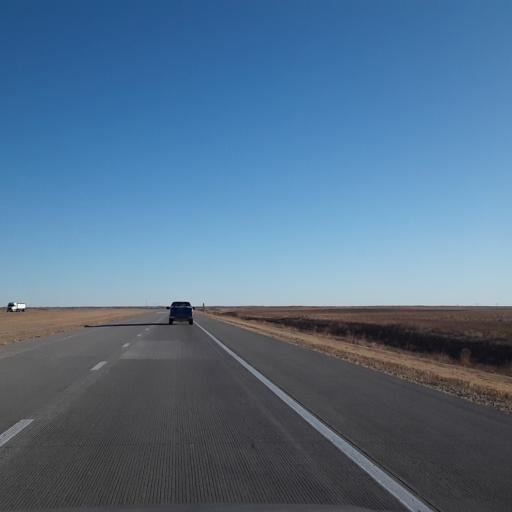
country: US
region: Kansas
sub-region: Seward County
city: Liberal
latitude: 37.1052
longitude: -100.7922
